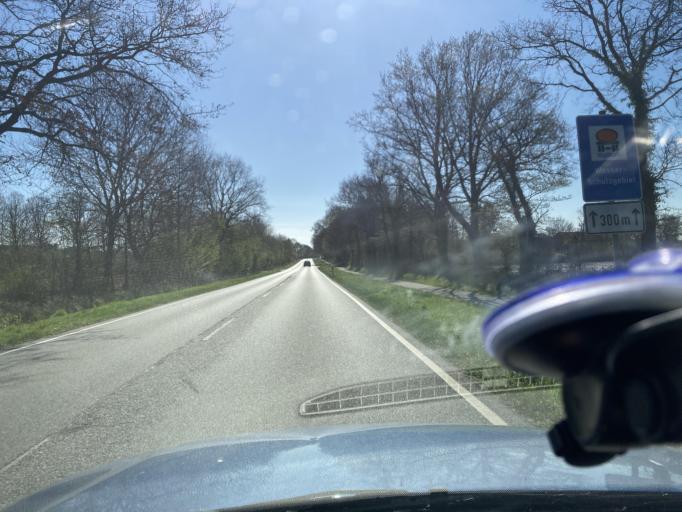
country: DE
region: Schleswig-Holstein
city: Ostrohe
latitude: 54.1938
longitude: 9.1497
